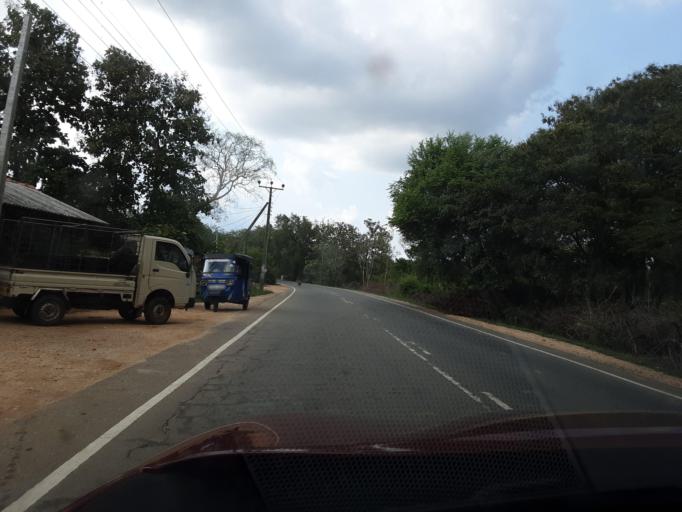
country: LK
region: Uva
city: Haputale
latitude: 6.5166
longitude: 81.1279
